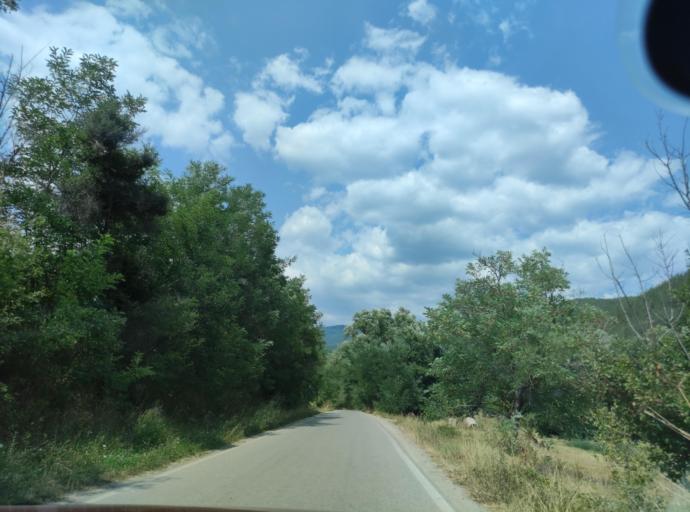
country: BG
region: Blagoevgrad
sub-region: Obshtina Belitsa
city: Belitsa
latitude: 41.9880
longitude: 23.5530
